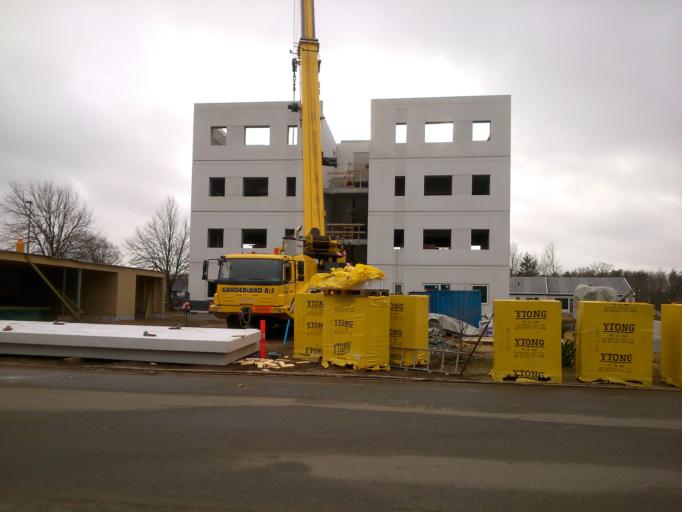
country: DK
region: Central Jutland
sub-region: Ringkobing-Skjern Kommune
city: Skjern
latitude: 55.9532
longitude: 8.4902
